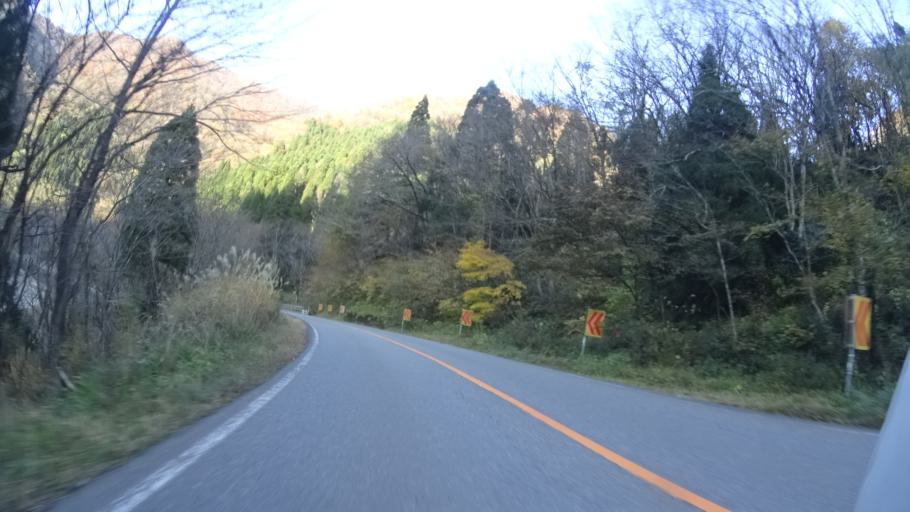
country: JP
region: Fukui
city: Ono
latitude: 35.9486
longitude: 136.6399
